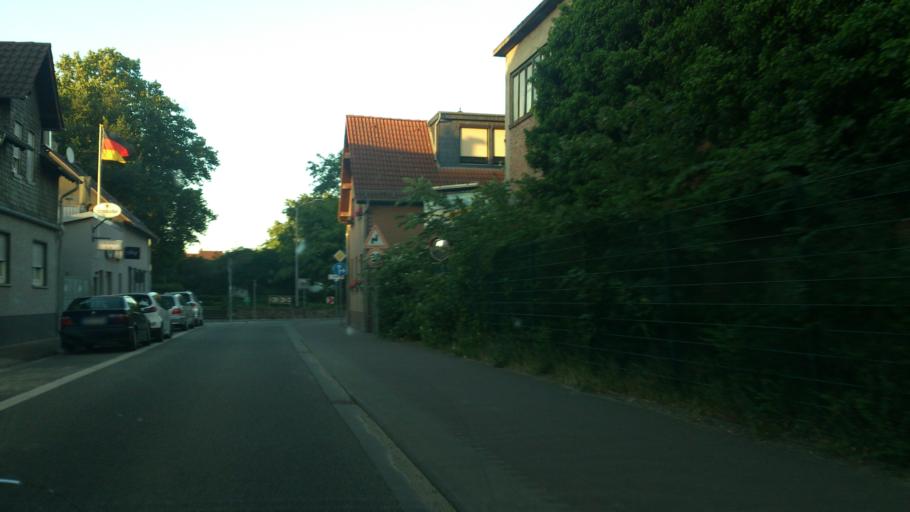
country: DE
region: Hesse
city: Kelsterbach
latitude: 50.0513
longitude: 8.4965
